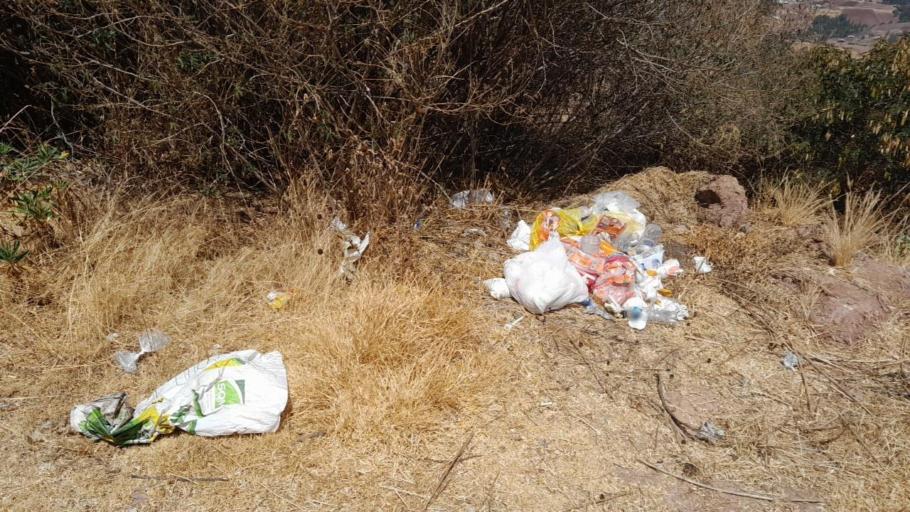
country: PE
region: Cusco
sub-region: Provincia de Cusco
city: Cusco
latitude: -13.4981
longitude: -71.9252
